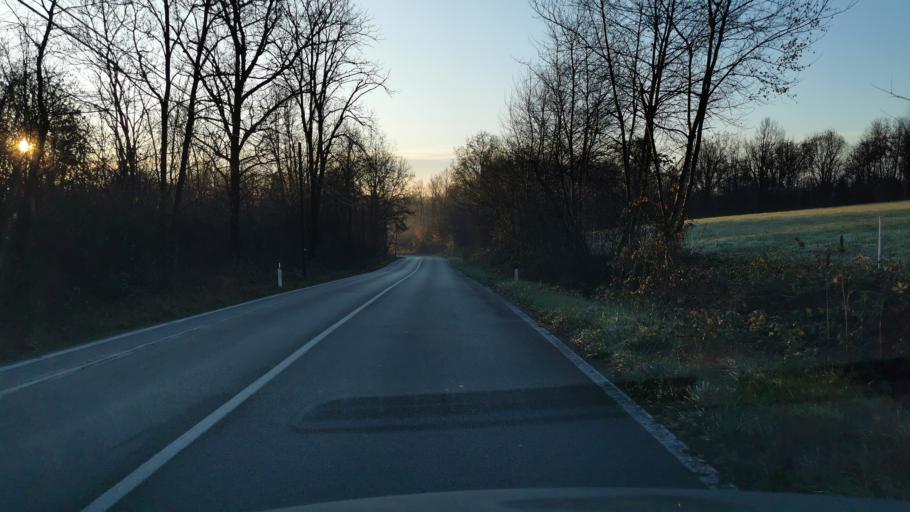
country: IT
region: Piedmont
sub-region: Provincia di Torino
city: La Cassa
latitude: 45.1641
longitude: 7.5276
